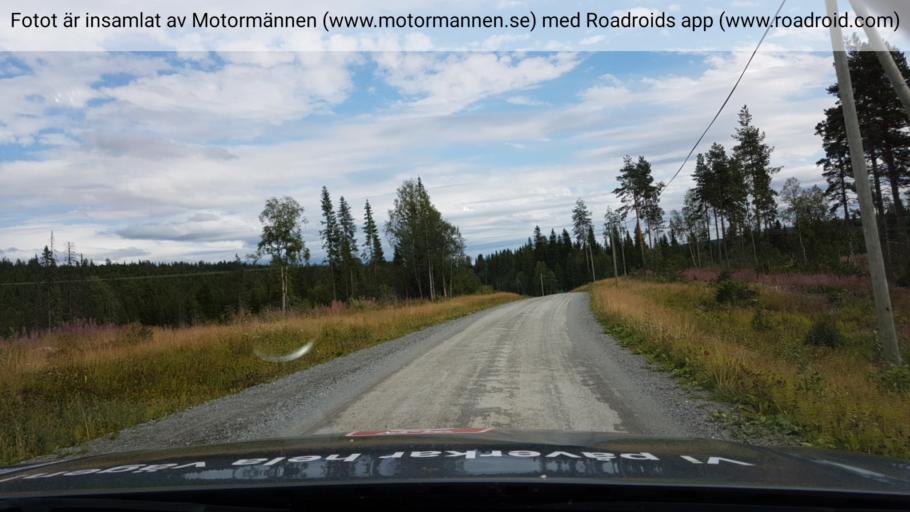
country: SE
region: Jaemtland
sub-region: Krokoms Kommun
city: Valla
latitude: 63.7130
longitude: 13.5317
